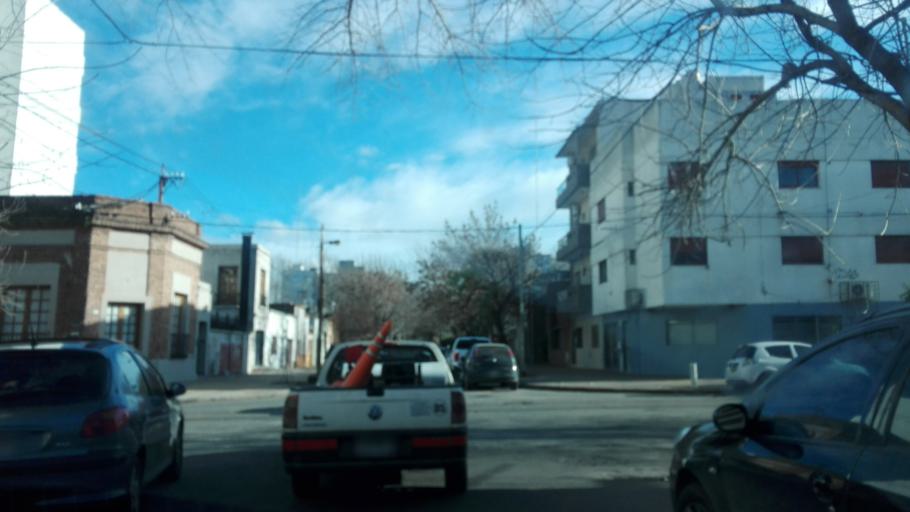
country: AR
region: Buenos Aires
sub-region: Partido de La Plata
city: La Plata
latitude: -34.9274
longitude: -57.9583
